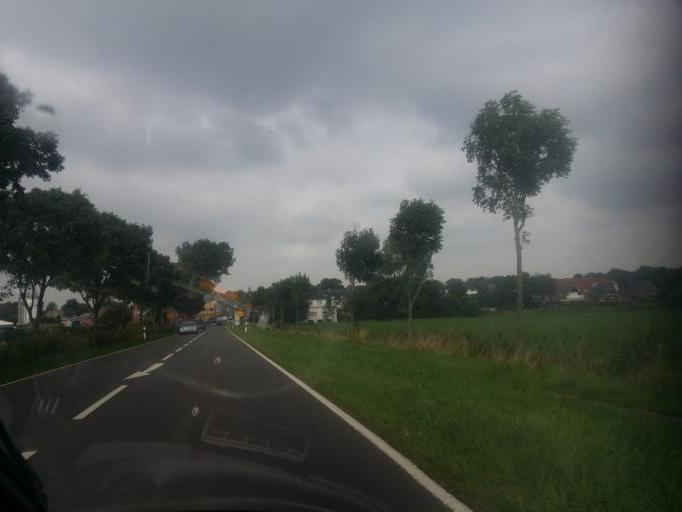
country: DE
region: Schleswig-Holstein
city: Husum
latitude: 54.4650
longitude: 9.0522
